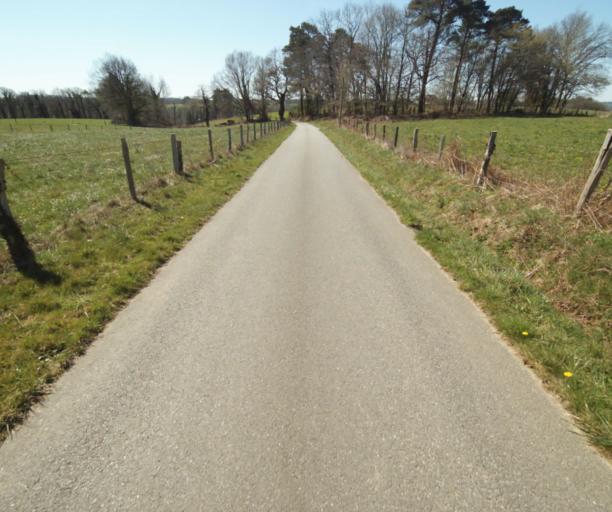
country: FR
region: Limousin
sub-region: Departement de la Correze
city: Chamboulive
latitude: 45.4600
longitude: 1.7102
